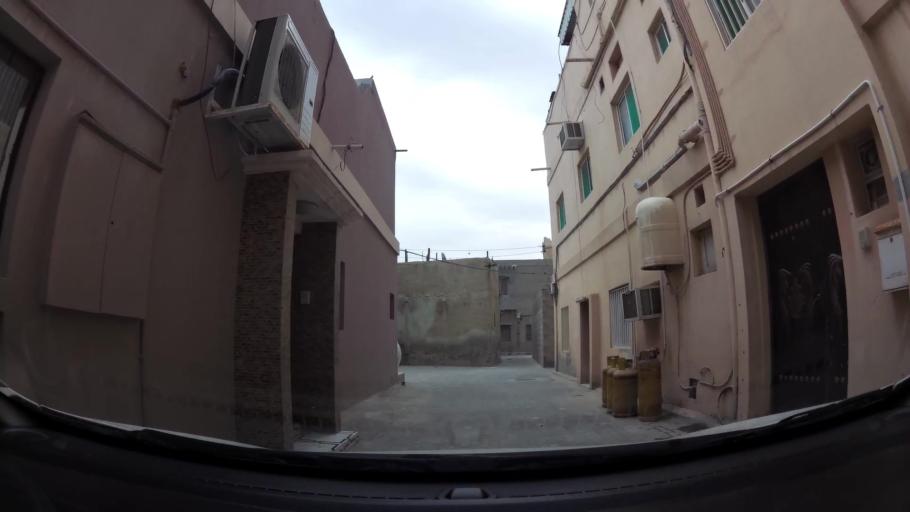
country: BH
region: Manama
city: Manama
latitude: 26.1848
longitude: 50.5836
